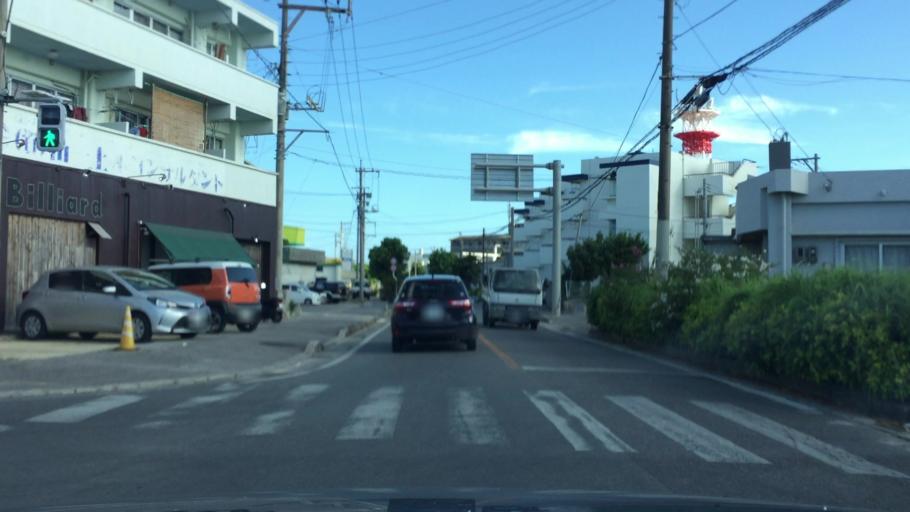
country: JP
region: Okinawa
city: Ishigaki
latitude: 24.3514
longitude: 124.1583
